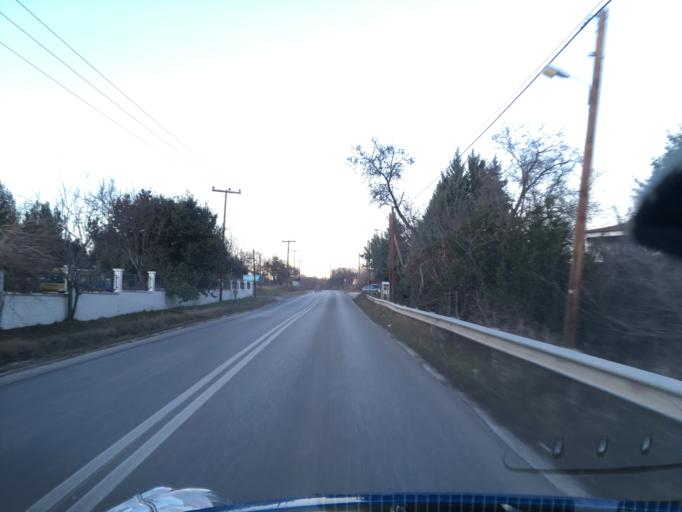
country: GR
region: West Macedonia
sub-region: Nomos Kozanis
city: Kozani
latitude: 40.2782
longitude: 21.7832
